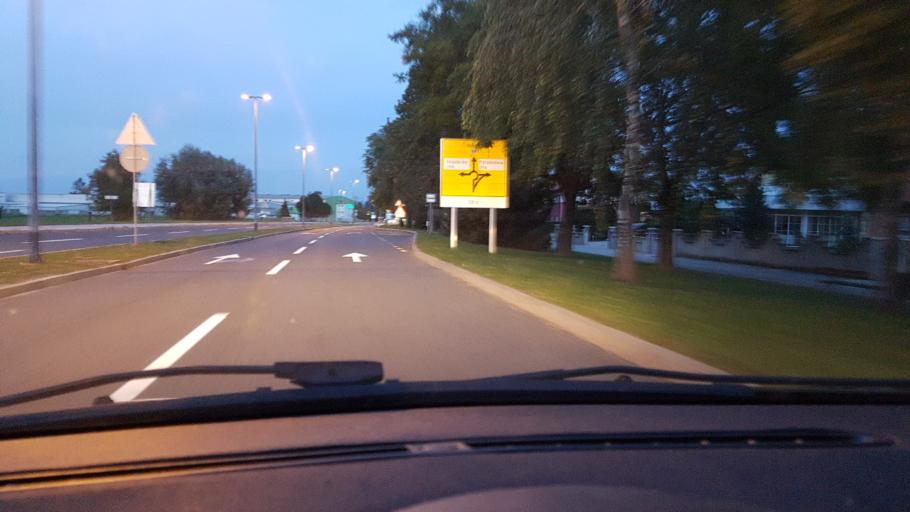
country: HR
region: Varazdinska
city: Ivanec
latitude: 46.2268
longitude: 16.1162
